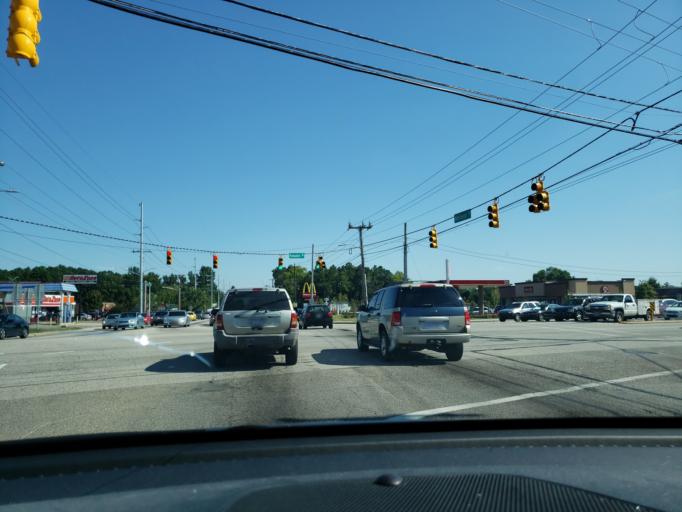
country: US
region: North Carolina
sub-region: Cumberland County
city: Fayetteville
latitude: 35.0973
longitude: -78.9159
